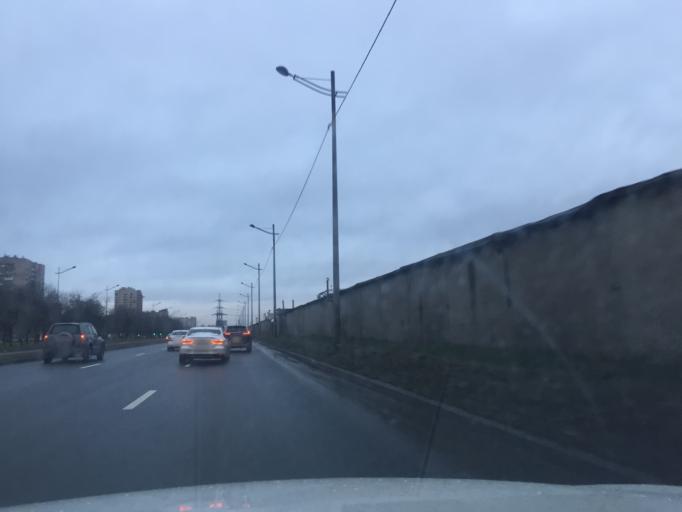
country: RU
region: St.-Petersburg
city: Kupchino
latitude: 59.8384
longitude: 30.3710
